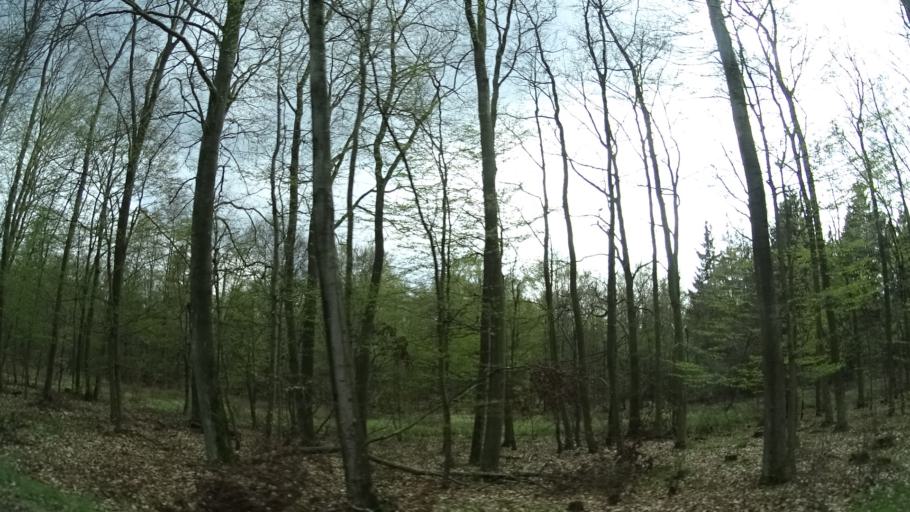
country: DE
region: Rheinland-Pfalz
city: Seesbach
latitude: 49.8716
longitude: 7.5567
